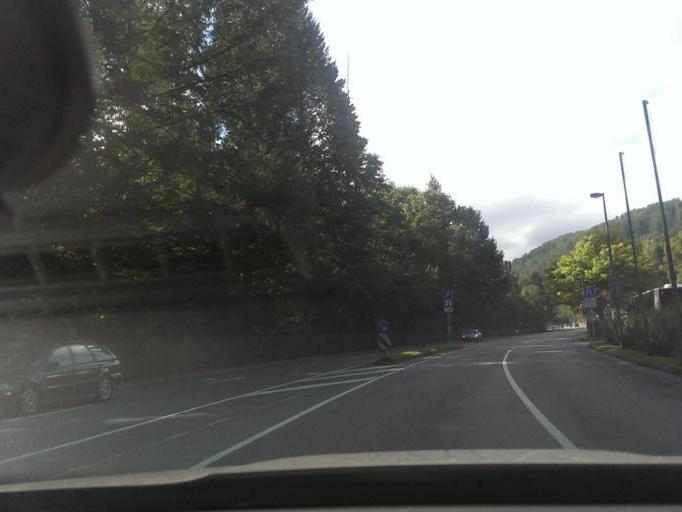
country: DE
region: Lower Saxony
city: Bad Harzburg
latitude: 51.8713
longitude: 10.5614
